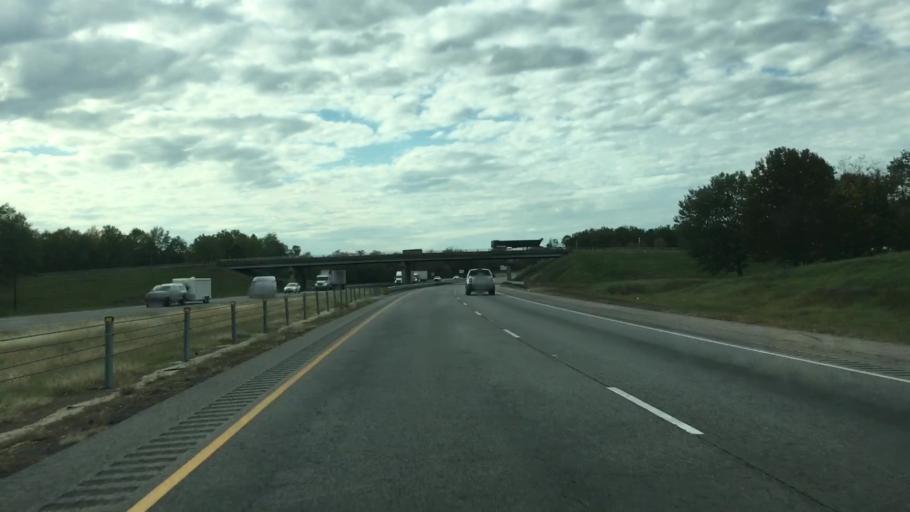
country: US
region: Arkansas
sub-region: Conway County
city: Morrilton
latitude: 35.1748
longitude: -92.7425
